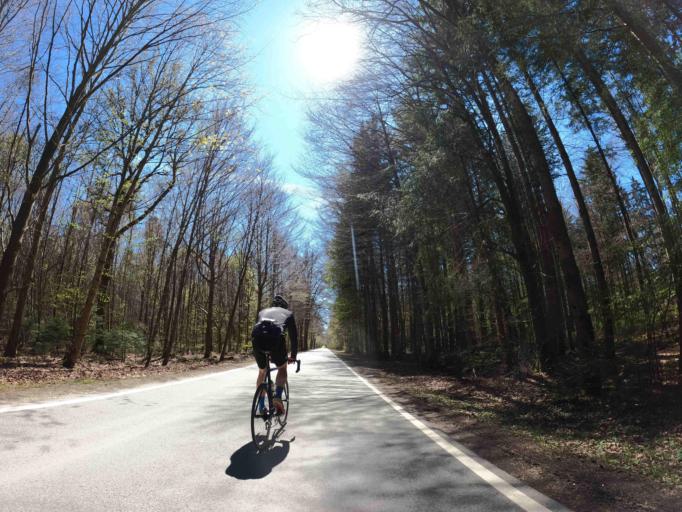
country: DE
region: Bavaria
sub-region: Upper Bavaria
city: Oberhaching
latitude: 48.0080
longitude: 11.5661
